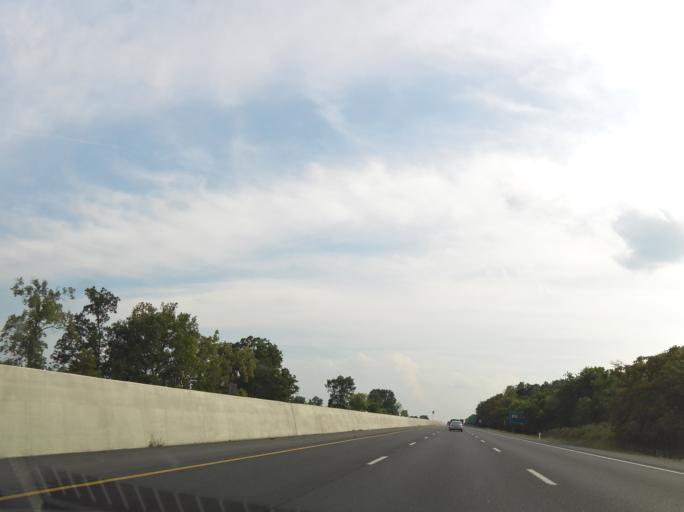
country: US
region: Maryland
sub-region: Washington County
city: Williamsport
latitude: 39.5552
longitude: -77.9063
